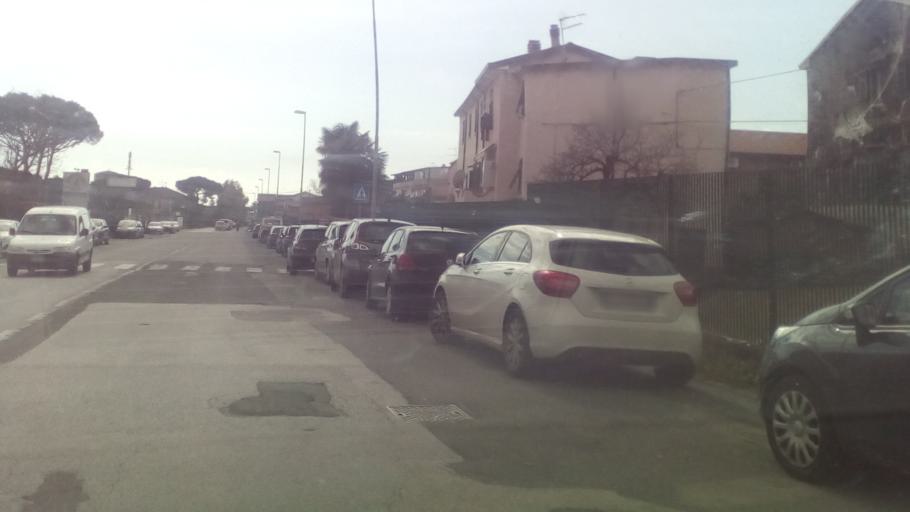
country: IT
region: Tuscany
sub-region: Provincia di Massa-Carrara
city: Carrara
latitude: 44.0523
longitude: 10.0757
